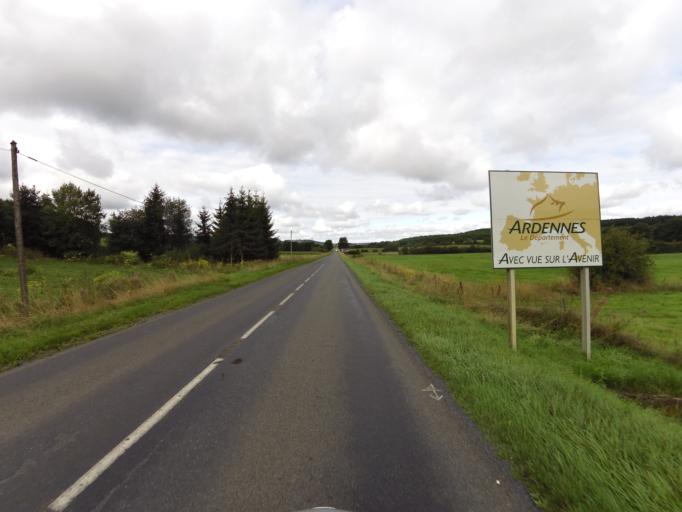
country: FR
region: Champagne-Ardenne
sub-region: Departement des Ardennes
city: Fromelennes
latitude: 50.1305
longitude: 4.8771
